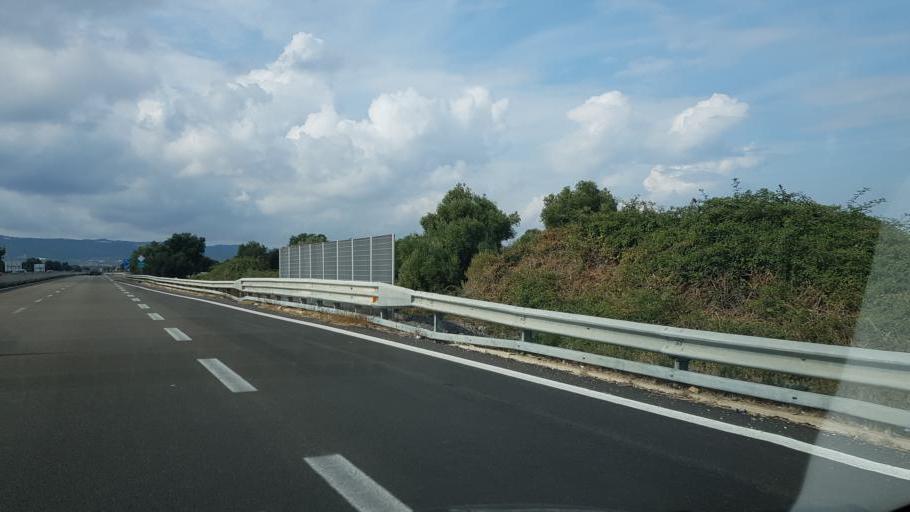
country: IT
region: Apulia
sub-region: Provincia di Brindisi
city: Pezze di Greco
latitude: 40.8339
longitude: 17.4051
